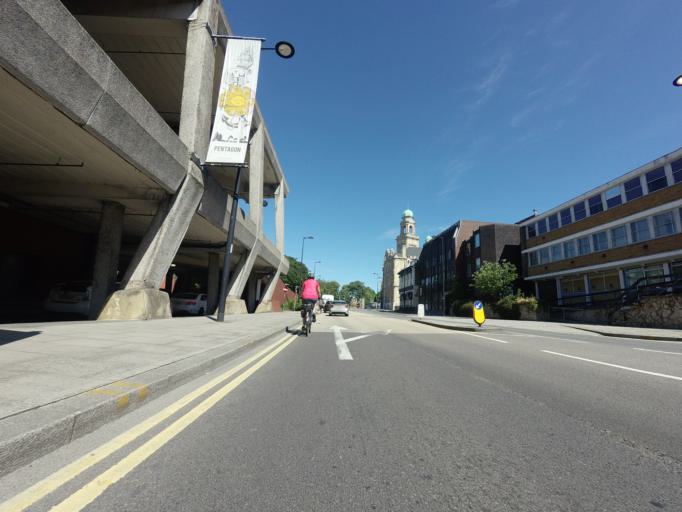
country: GB
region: England
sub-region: Kent
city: Chatham
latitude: 51.3843
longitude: 0.5262
